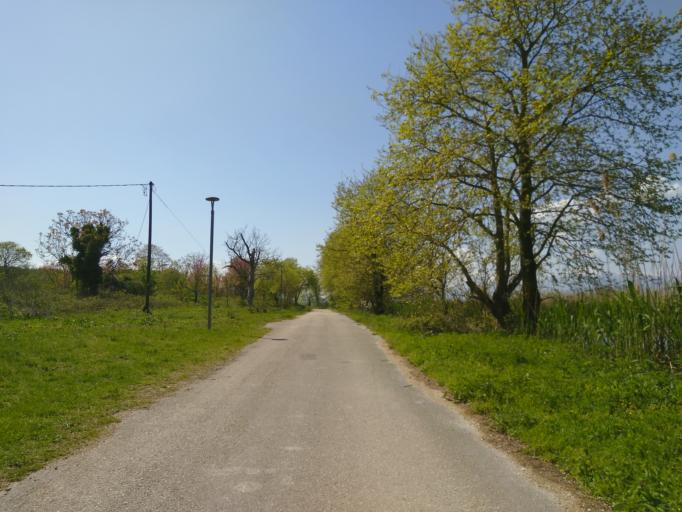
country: GR
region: Epirus
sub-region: Nomos Ioanninon
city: Ioannina
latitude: 39.6765
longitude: 20.8730
